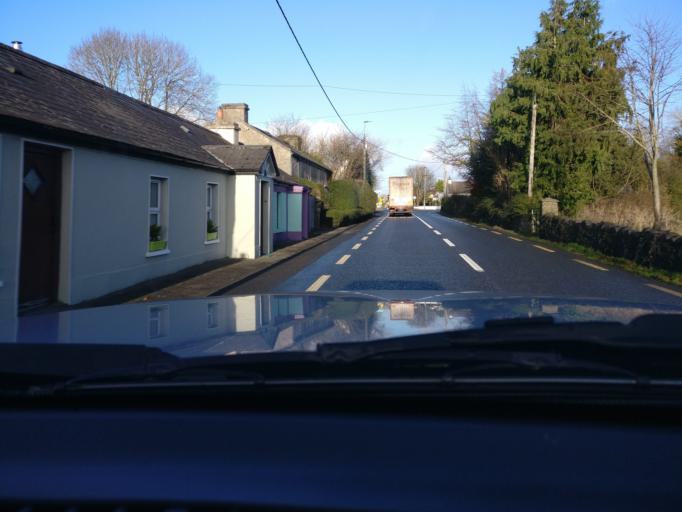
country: IE
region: Leinster
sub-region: An Mhi
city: Athboy
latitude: 53.6632
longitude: -7.0199
